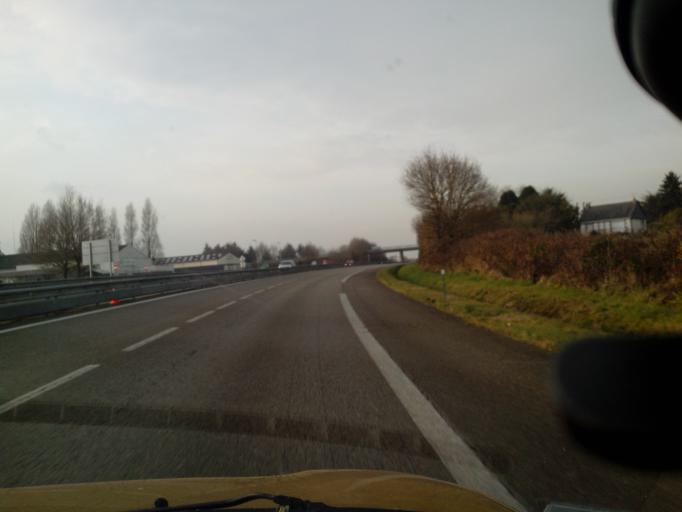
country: FR
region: Brittany
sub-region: Departement du Morbihan
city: Josselin
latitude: 47.9510
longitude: -2.5277
